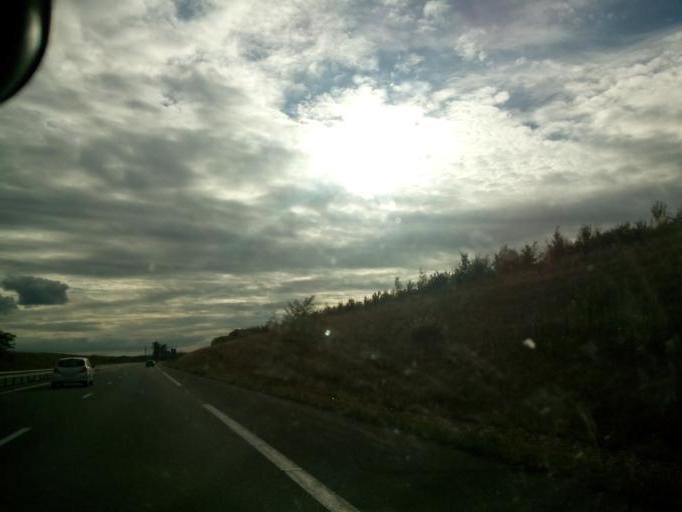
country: FR
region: Centre
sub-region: Departement d'Indre-et-Loire
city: Montbazon
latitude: 47.3057
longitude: 0.7079
